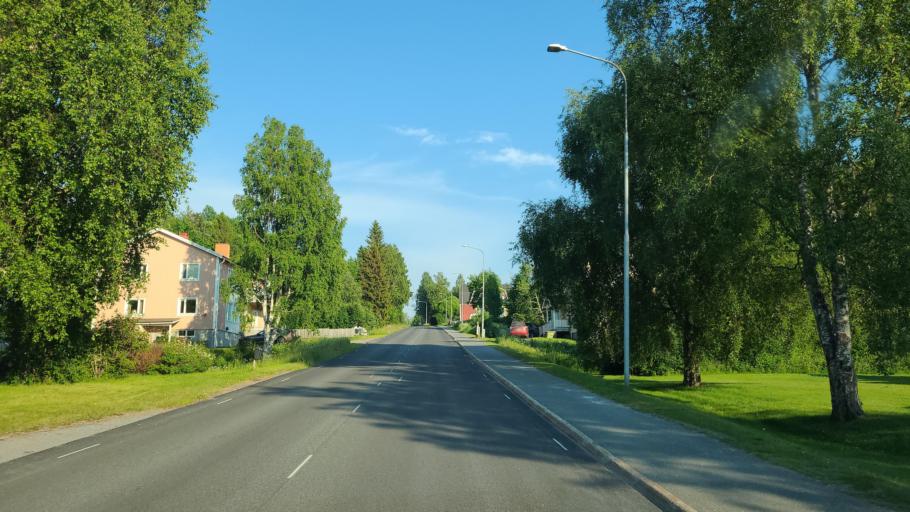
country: SE
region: Vaesterbotten
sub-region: Skelleftea Kommun
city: Burea
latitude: 64.3677
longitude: 21.3225
